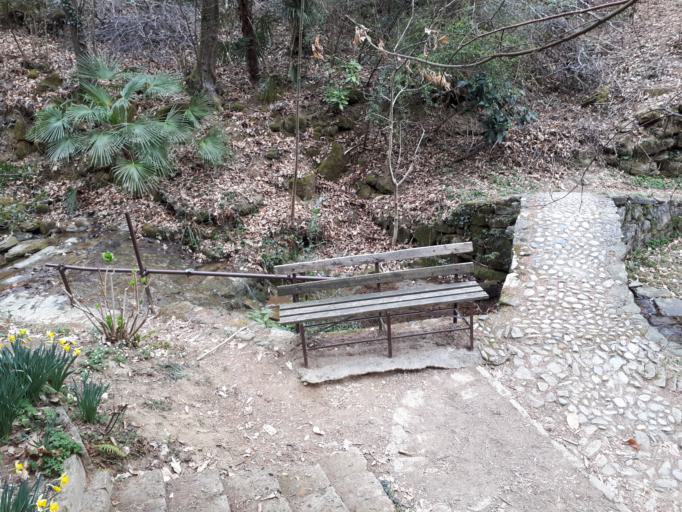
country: IT
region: Lombardy
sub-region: Provincia di Lecco
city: Santa Maria Hoe
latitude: 45.7461
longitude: 9.3825
